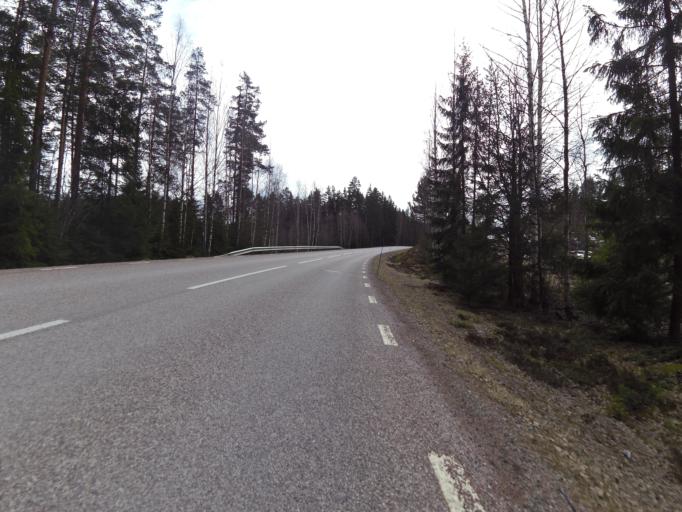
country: SE
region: Dalarna
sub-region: Hedemora Kommun
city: Langshyttan
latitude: 60.5327
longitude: 16.1316
